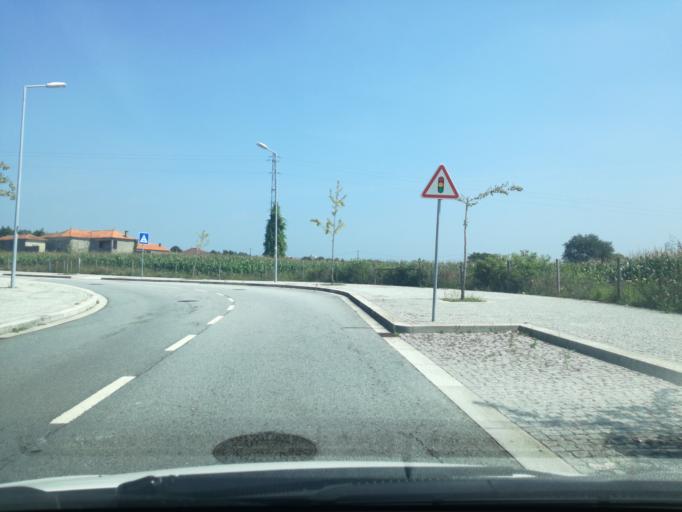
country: PT
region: Porto
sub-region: Maia
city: Gemunde
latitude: 41.2462
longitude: -8.6586
